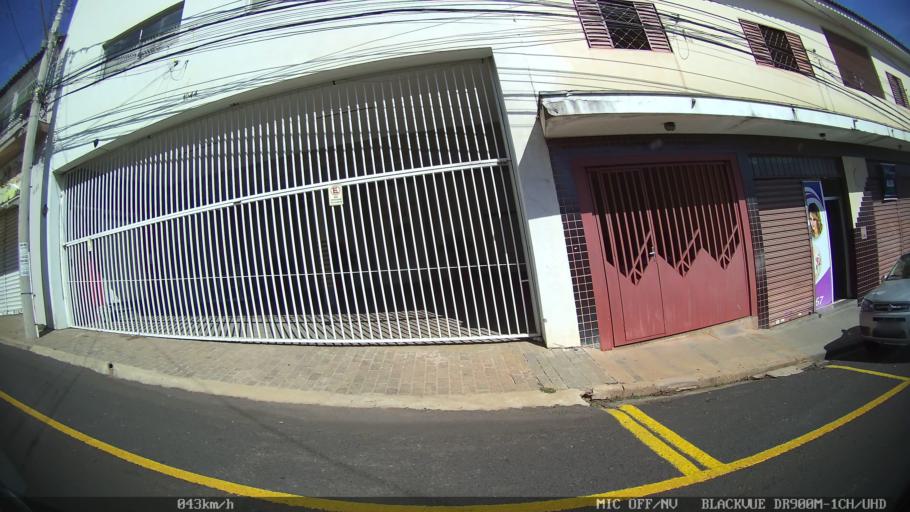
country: BR
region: Sao Paulo
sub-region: Franca
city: Franca
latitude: -20.5348
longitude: -47.4050
